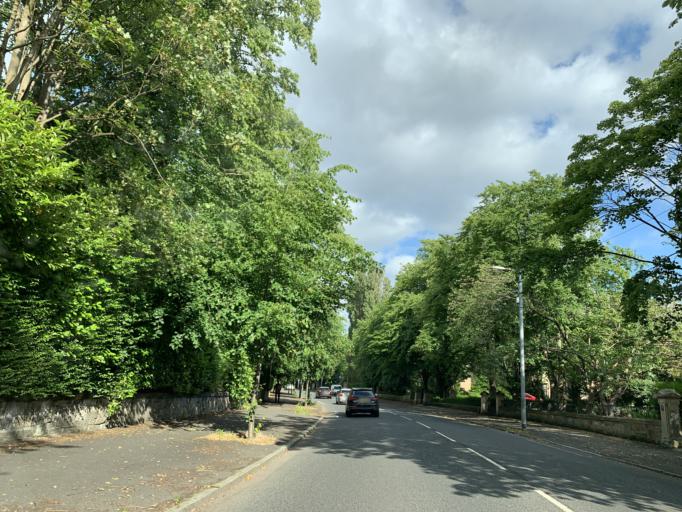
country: GB
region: Scotland
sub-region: Glasgow City
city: Glasgow
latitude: 55.8417
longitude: -4.2873
